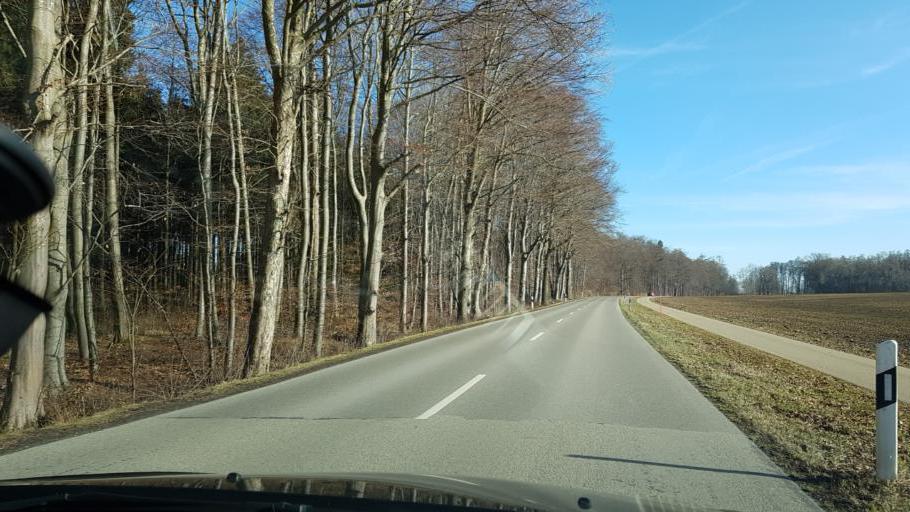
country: DE
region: Bavaria
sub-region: Upper Bavaria
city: Oberschweinbach
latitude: 48.2256
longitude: 11.1731
